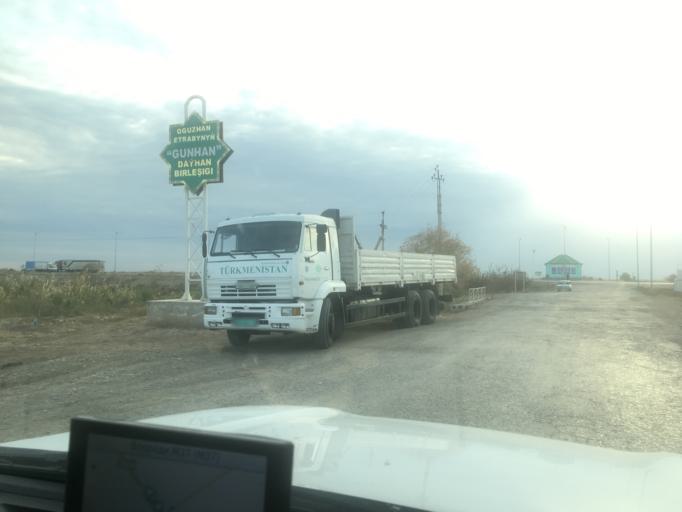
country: TM
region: Ahal
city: Tejen
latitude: 37.3468
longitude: 60.7367
